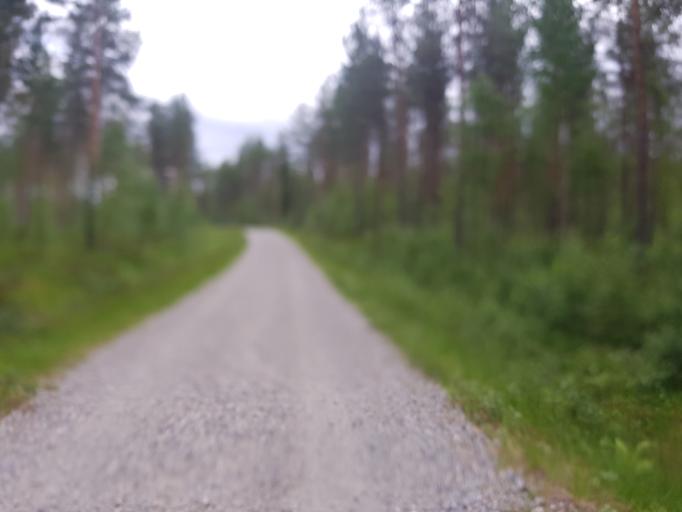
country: FI
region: Kainuu
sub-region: Kehys-Kainuu
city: Kuhmo
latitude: 64.4517
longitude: 29.7185
